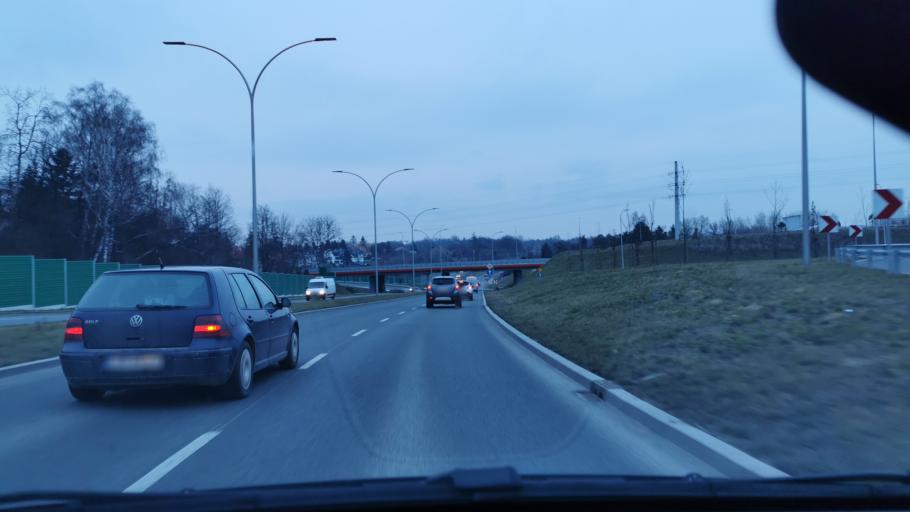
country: PL
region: Lublin Voivodeship
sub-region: Powiat lubelski
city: Lublin
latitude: 51.2502
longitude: 22.5048
